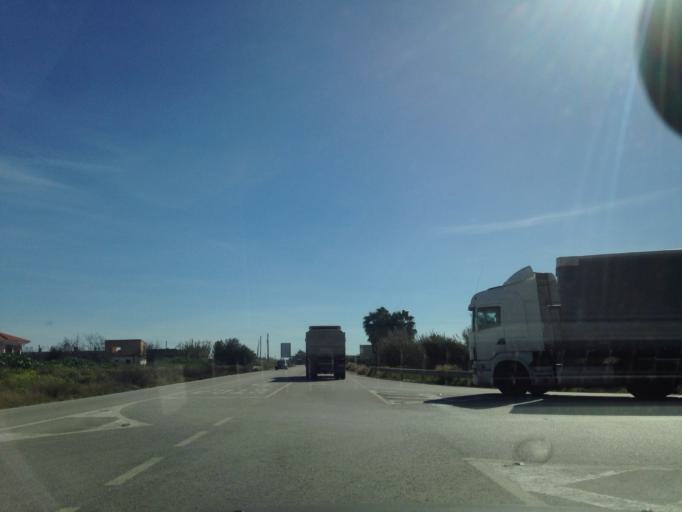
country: ES
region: Andalusia
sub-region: Provincia de Malaga
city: Alhaurin de la Torre
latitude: 36.7110
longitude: -4.5260
